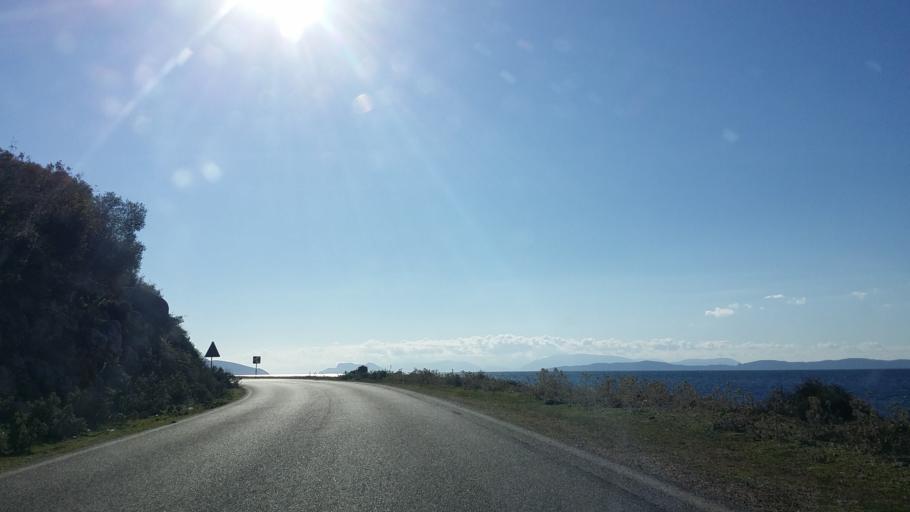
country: GR
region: West Greece
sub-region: Nomos Aitolias kai Akarnanias
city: Kandila
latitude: 38.7077
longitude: 20.8952
